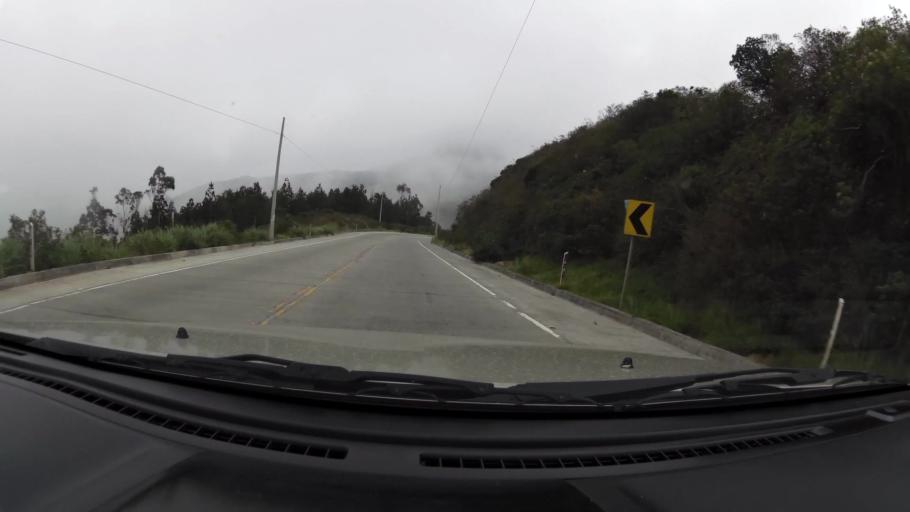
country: EC
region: Canar
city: Canar
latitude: -2.4836
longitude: -79.0004
